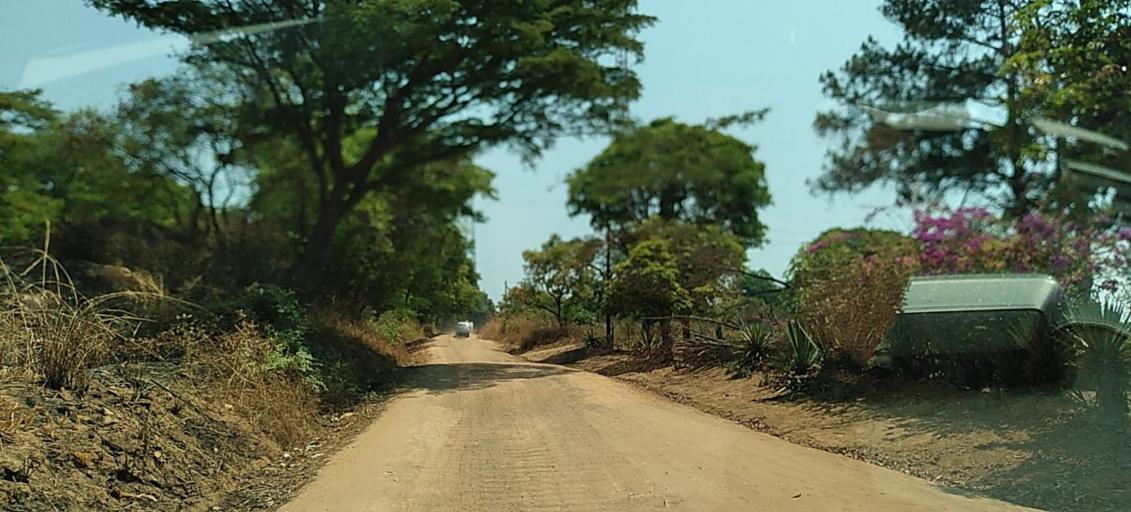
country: ZM
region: Copperbelt
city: Chingola
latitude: -12.6002
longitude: 27.9556
